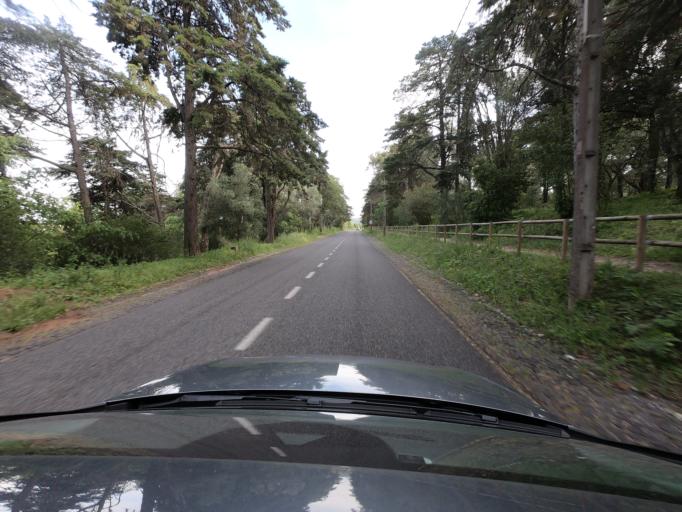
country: PT
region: Setubal
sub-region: Almada
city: Pragal
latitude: 38.7166
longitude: -9.1799
